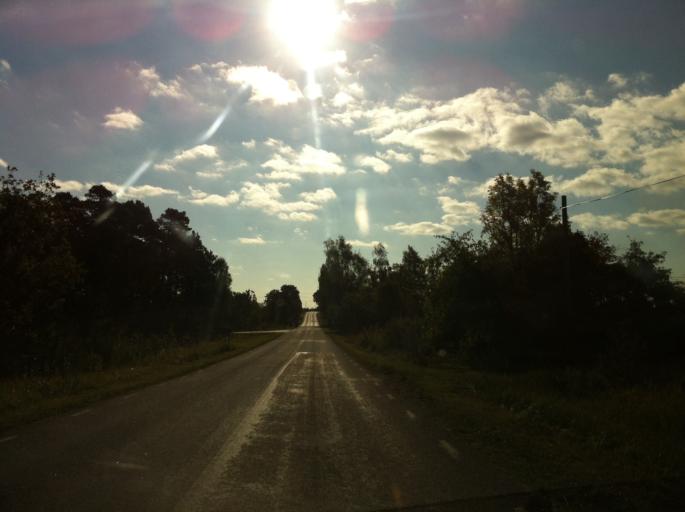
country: SE
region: Gotland
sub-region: Gotland
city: Slite
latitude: 57.4537
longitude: 18.7011
